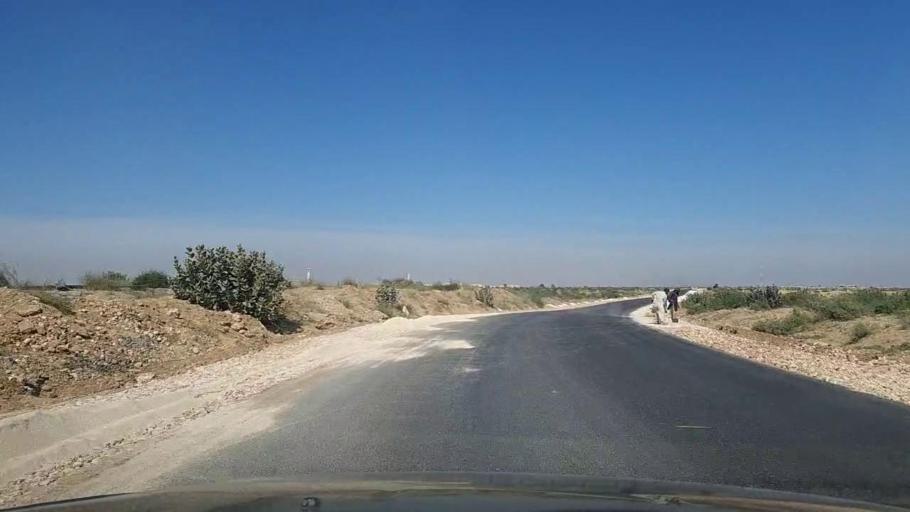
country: PK
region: Sindh
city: Kotri
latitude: 25.3067
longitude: 68.2033
